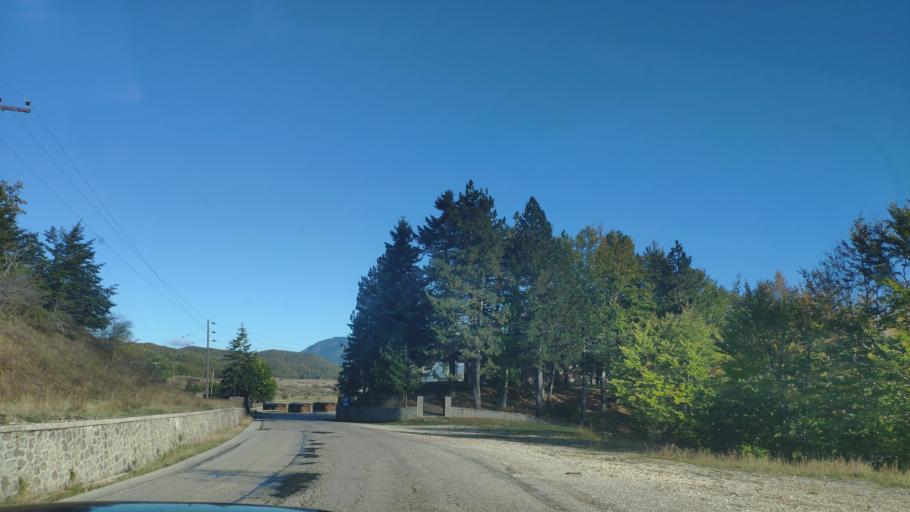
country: GR
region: Epirus
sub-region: Nomos Ioanninon
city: Metsovo
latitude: 39.7835
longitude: 21.1598
